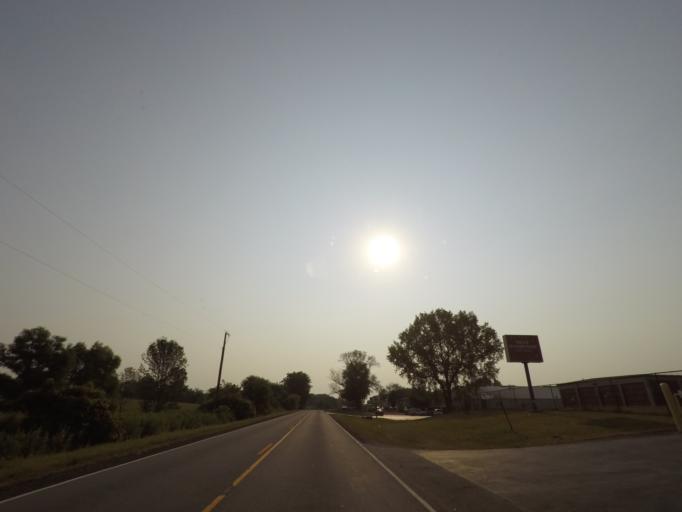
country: US
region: Wisconsin
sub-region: Dane County
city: McFarland
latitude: 43.0523
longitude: -89.2599
